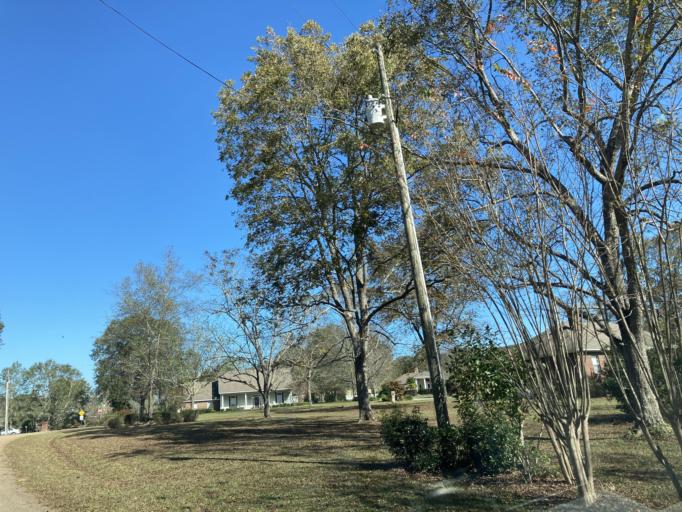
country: US
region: Mississippi
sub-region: Lamar County
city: West Hattiesburg
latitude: 31.2678
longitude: -89.4191
